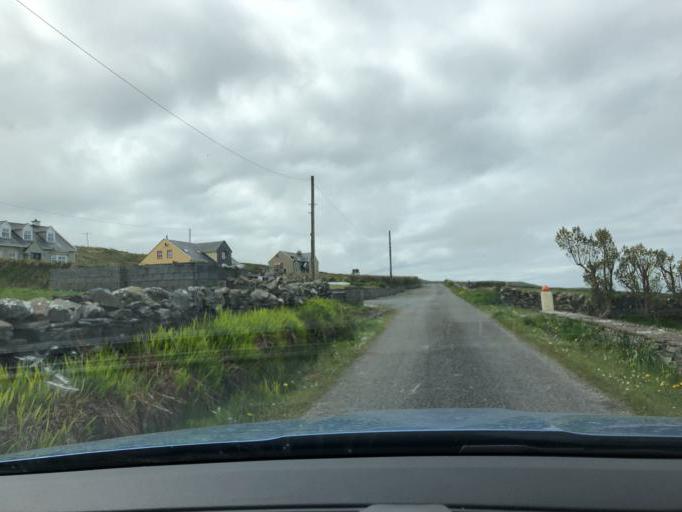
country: IE
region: Connaught
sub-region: County Galway
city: Bearna
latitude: 52.9959
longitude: -9.4014
